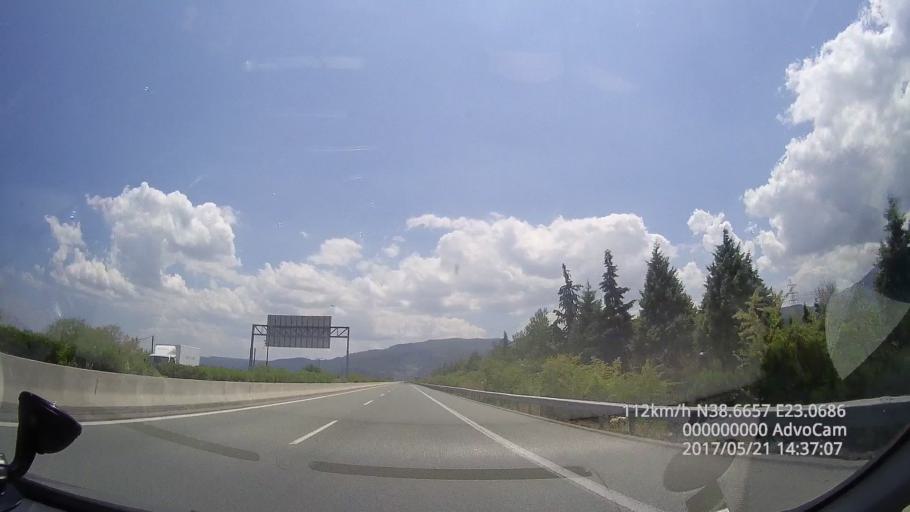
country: GR
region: Central Greece
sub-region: Nomos Fthiotidos
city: Livanates
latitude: 38.6627
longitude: 23.0703
